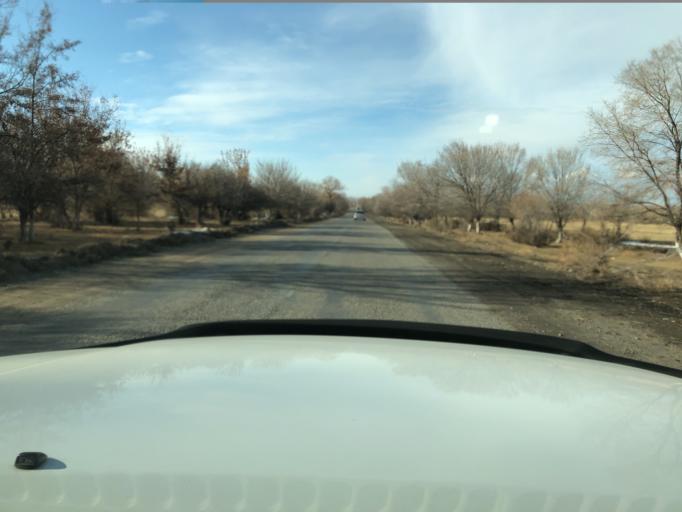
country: KG
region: Ysyk-Koel
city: Pokrovka
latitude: 42.3292
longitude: 77.9628
